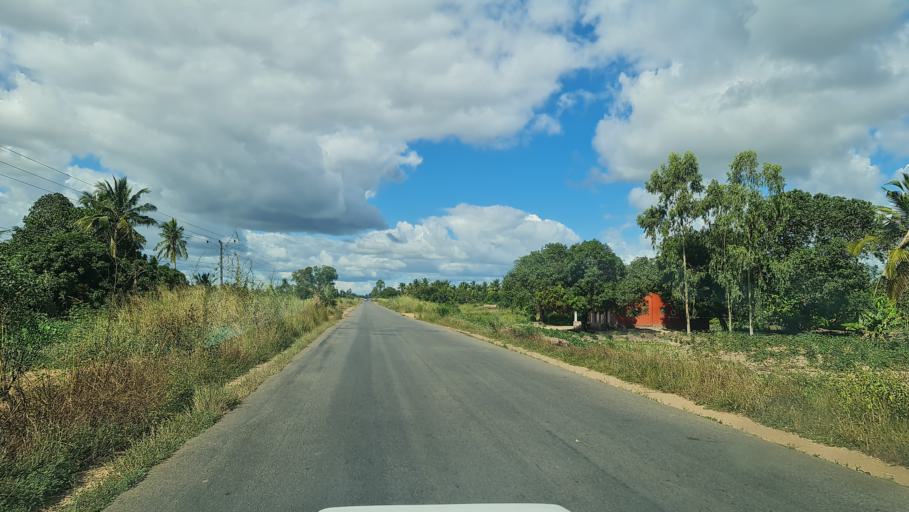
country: MZ
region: Zambezia
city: Quelimane
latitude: -17.5879
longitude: 36.7551
